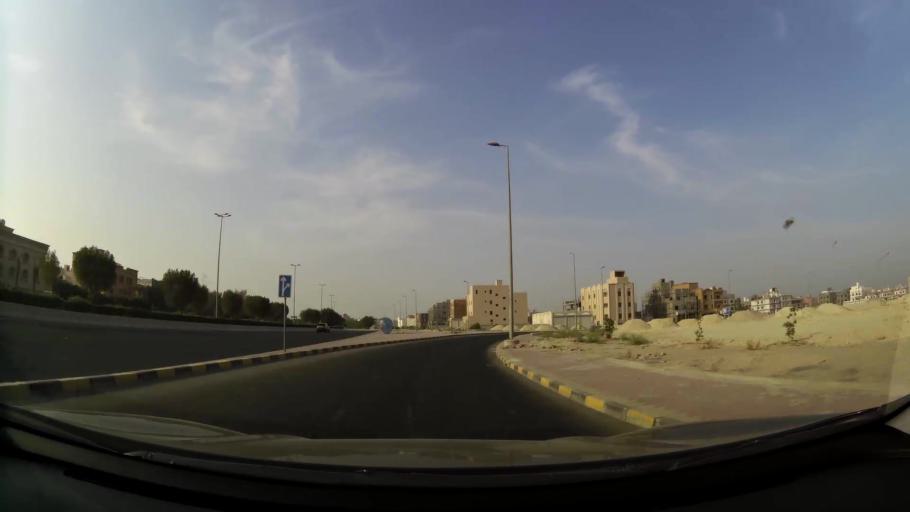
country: KW
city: Al Funaytis
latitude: 29.2184
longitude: 48.0882
